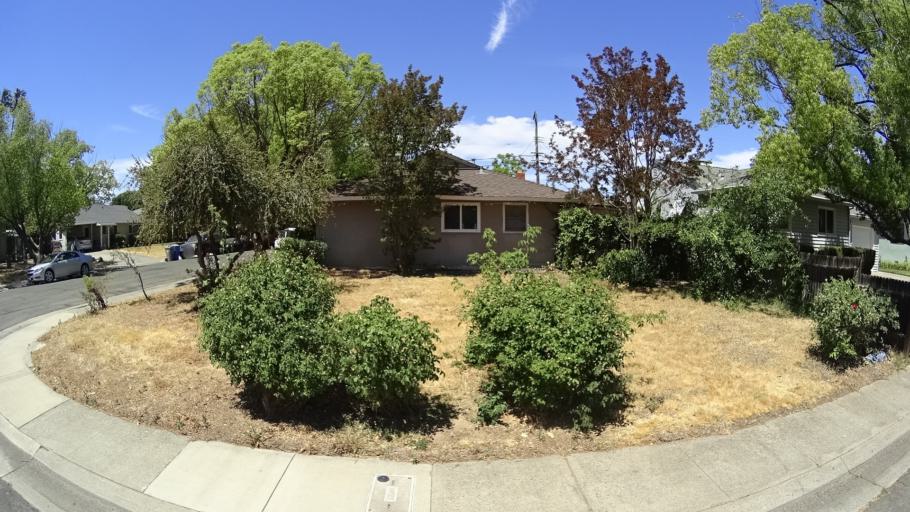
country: US
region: California
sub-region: Sacramento County
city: Florin
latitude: 38.5182
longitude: -121.4303
